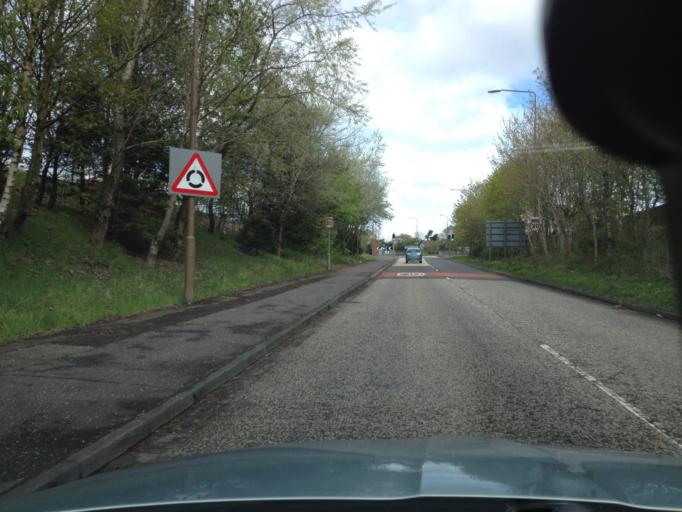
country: GB
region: Scotland
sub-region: West Lothian
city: Livingston
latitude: 55.8881
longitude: -3.5504
